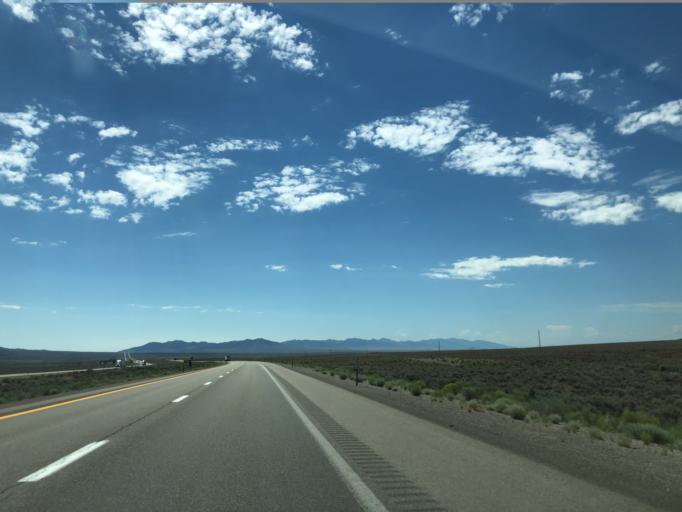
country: US
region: Nevada
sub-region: Elko County
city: Wells
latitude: 41.0389
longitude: -114.5020
